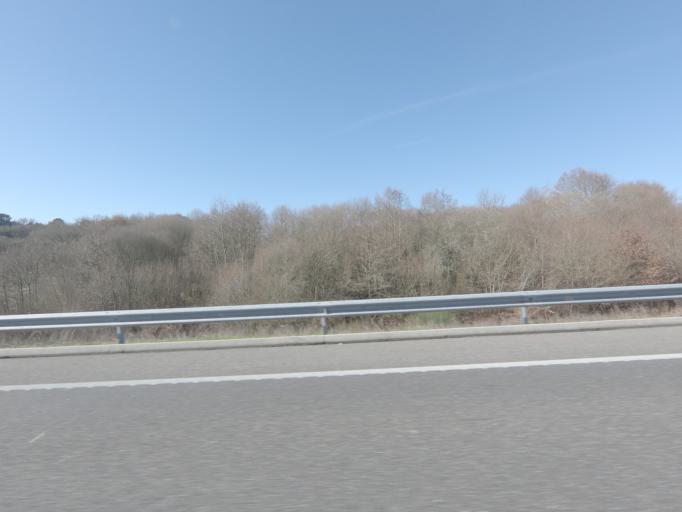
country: ES
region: Galicia
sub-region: Provincia de Ourense
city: Maside
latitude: 42.4275
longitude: -8.0129
